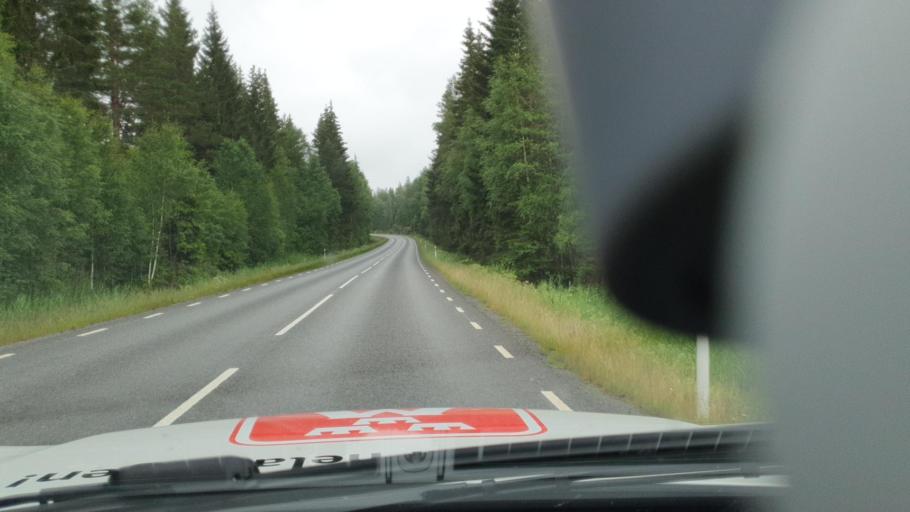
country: SE
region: OErebro
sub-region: Degerfors Kommun
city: Degerfors
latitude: 59.2227
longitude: 14.3673
